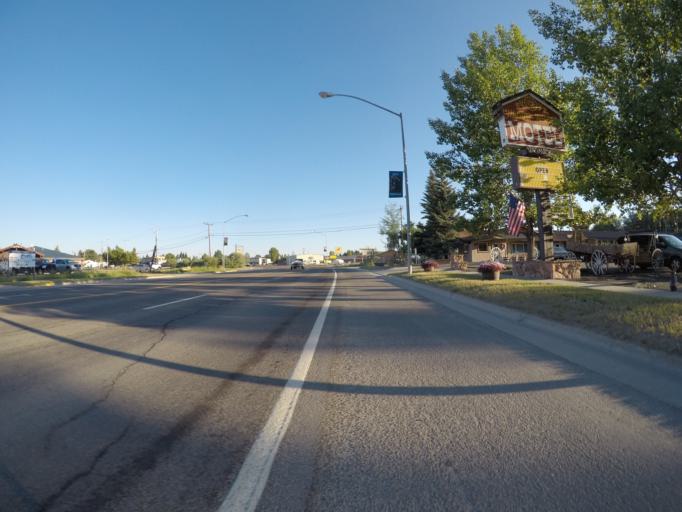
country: US
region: Wyoming
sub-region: Sublette County
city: Pinedale
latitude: 42.8651
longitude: -109.8544
